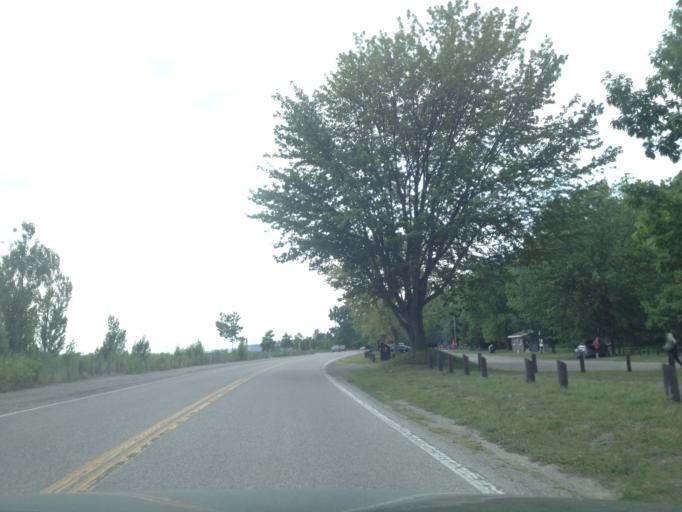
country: CA
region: Ontario
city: Aylmer
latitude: 42.6547
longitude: -81.0111
